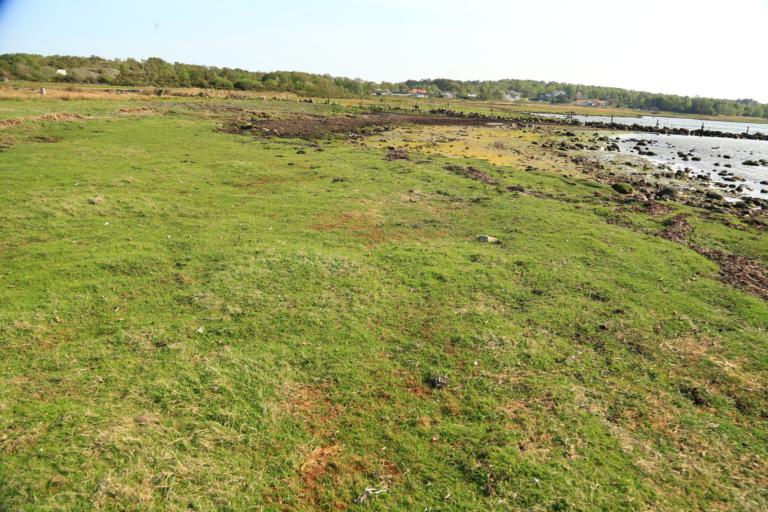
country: SE
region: Halland
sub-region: Varbergs Kommun
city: Varberg
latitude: 57.1565
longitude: 12.2278
